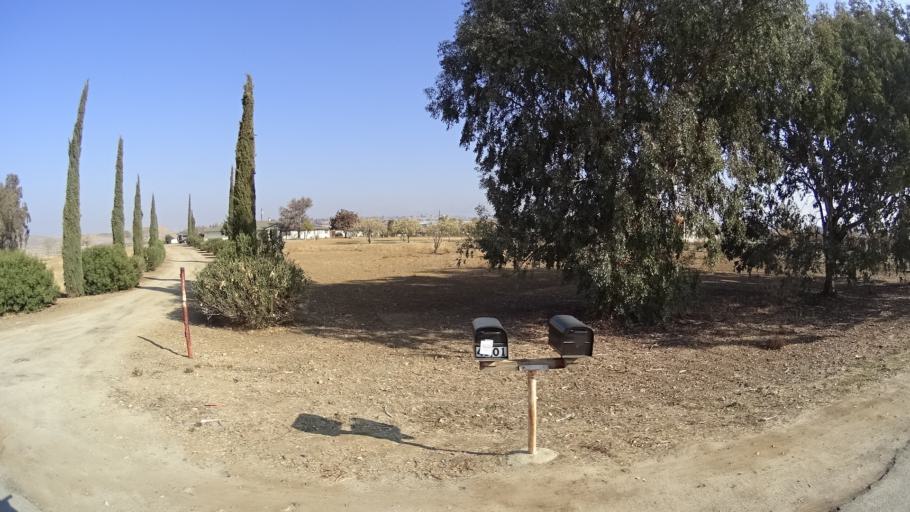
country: US
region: California
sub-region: Kern County
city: Lamont
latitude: 35.4079
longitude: -118.8629
